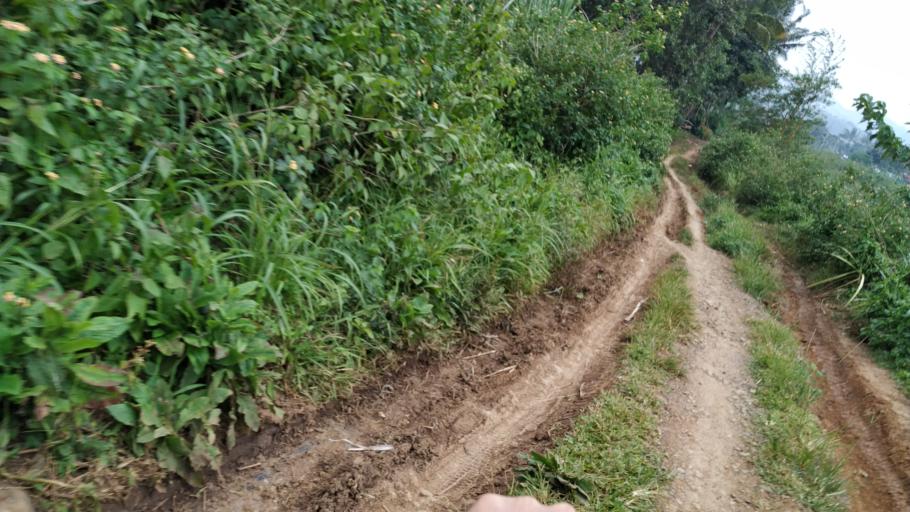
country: PH
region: Western Visayas
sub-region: Province of Negros Occidental
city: Quezon
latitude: 10.4226
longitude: 123.2391
